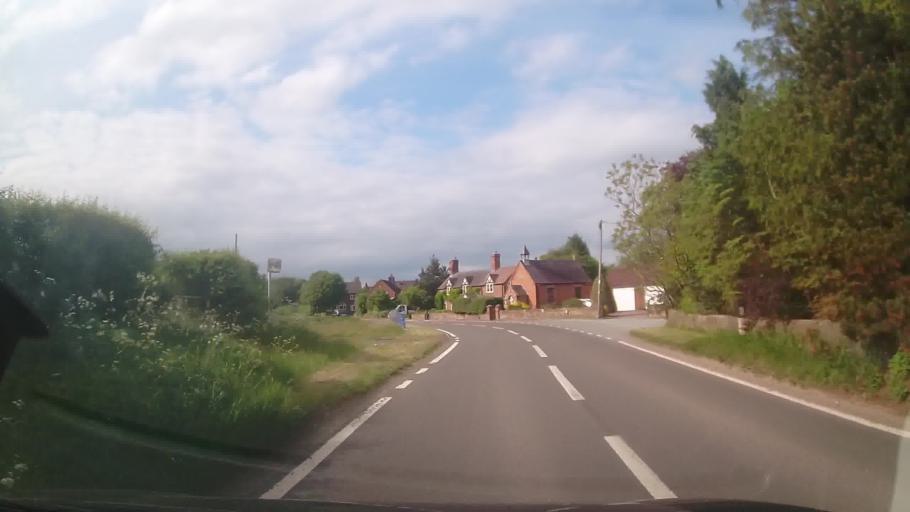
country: GB
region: England
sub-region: Shropshire
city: Petton
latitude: 52.8275
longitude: -2.8059
